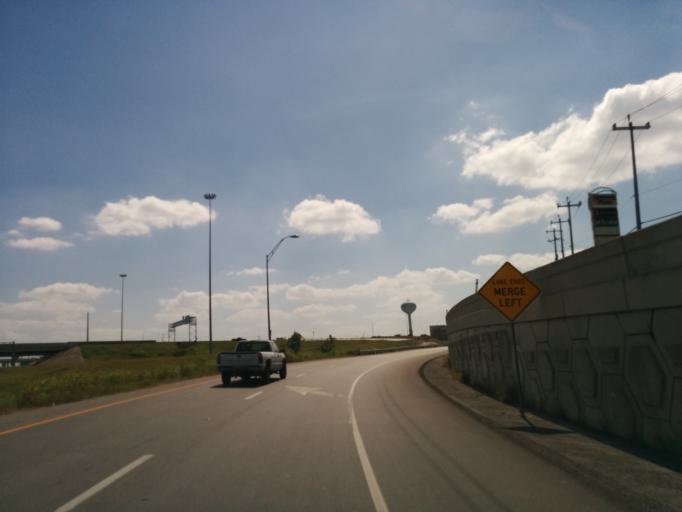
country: US
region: Texas
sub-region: Bexar County
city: Live Oak
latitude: 29.5698
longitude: -98.3317
